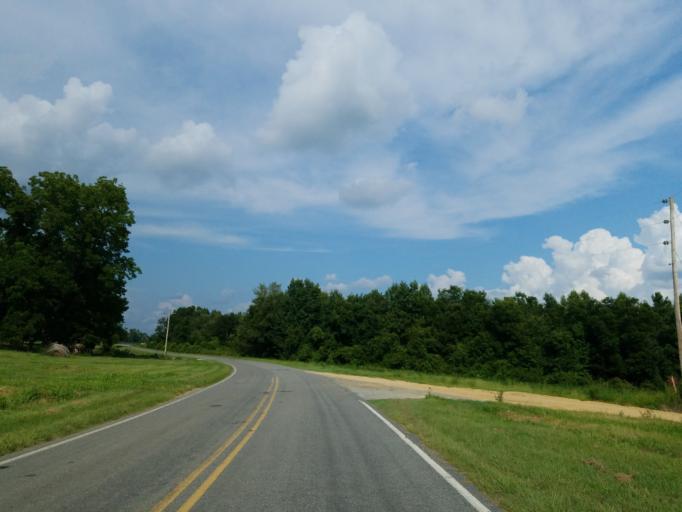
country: US
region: Georgia
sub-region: Dooly County
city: Unadilla
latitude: 32.1911
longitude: -83.7381
